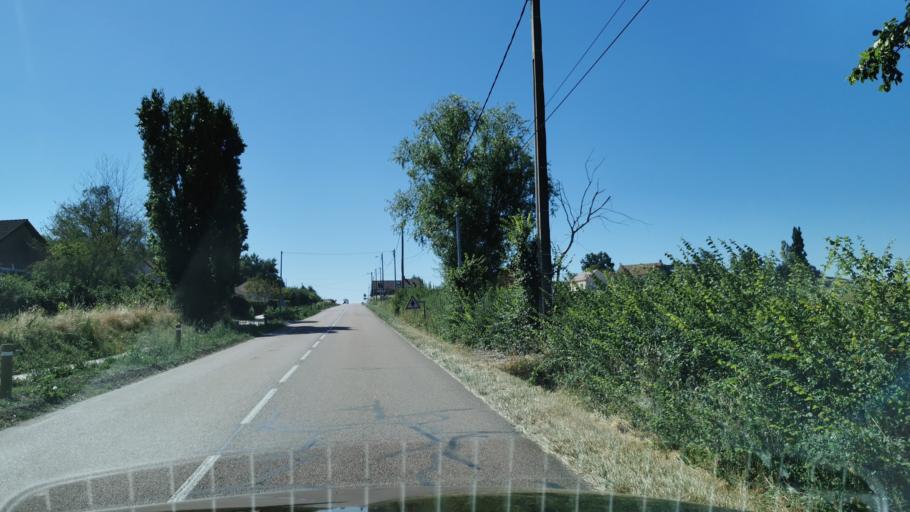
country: FR
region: Bourgogne
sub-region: Departement de Saone-et-Loire
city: Ecuisses
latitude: 46.7338
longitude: 4.5648
